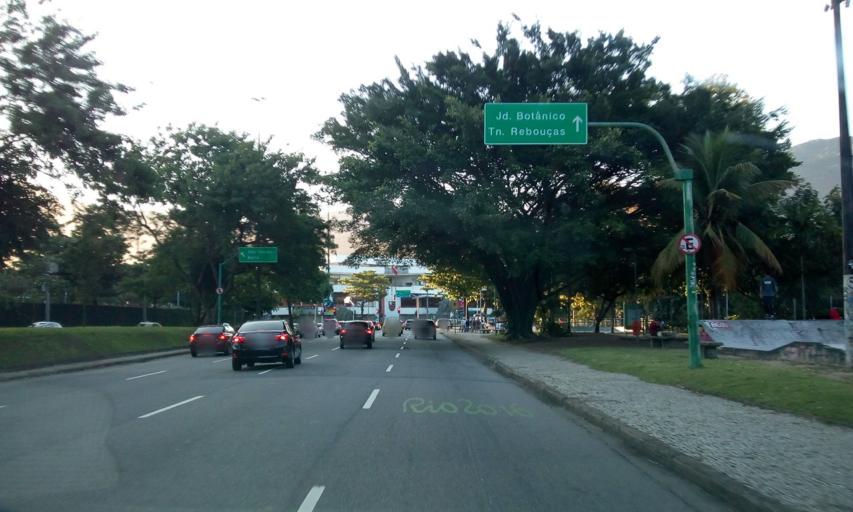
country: BR
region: Rio de Janeiro
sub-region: Rio De Janeiro
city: Rio de Janeiro
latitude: -22.9793
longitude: -43.2167
